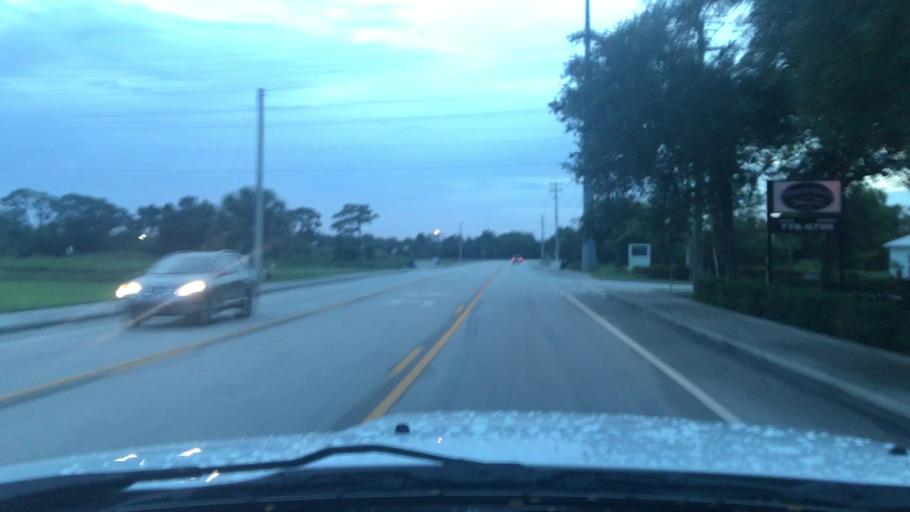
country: US
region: Florida
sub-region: Indian River County
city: Florida Ridge
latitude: 27.6031
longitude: -80.3864
